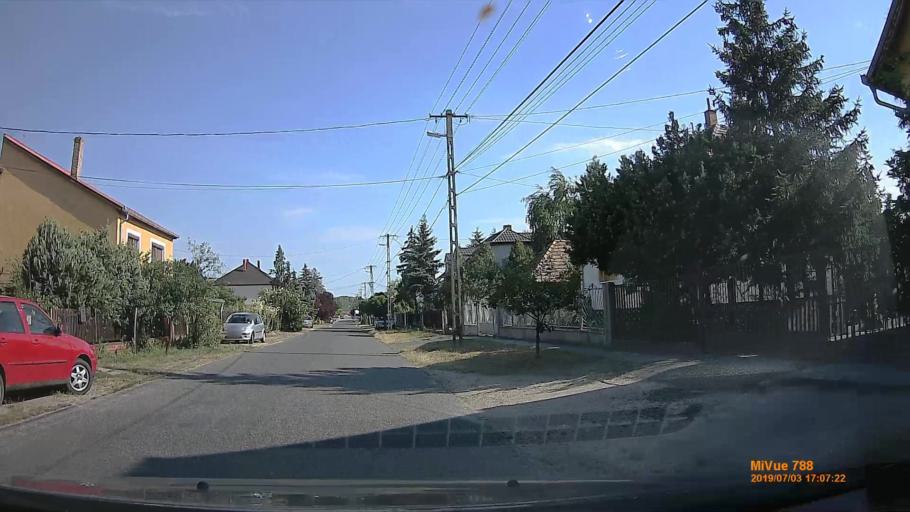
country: HU
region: Gyor-Moson-Sopron
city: Gyor
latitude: 47.7197
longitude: 17.6501
